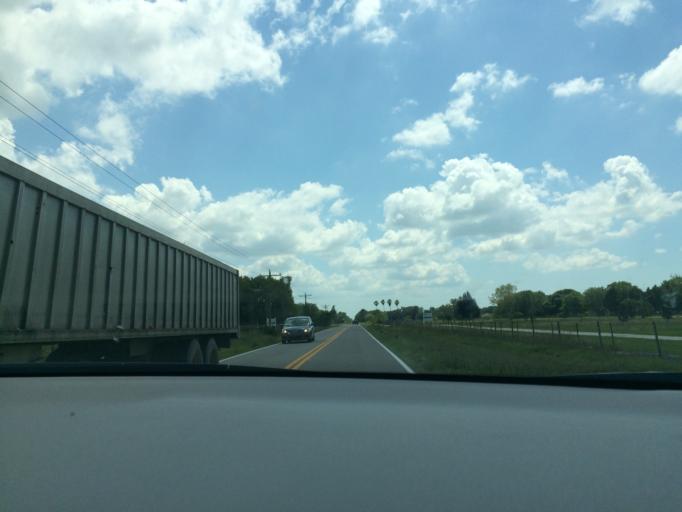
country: US
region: Florida
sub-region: Sarasota County
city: The Meadows
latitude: 27.4698
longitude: -82.3956
